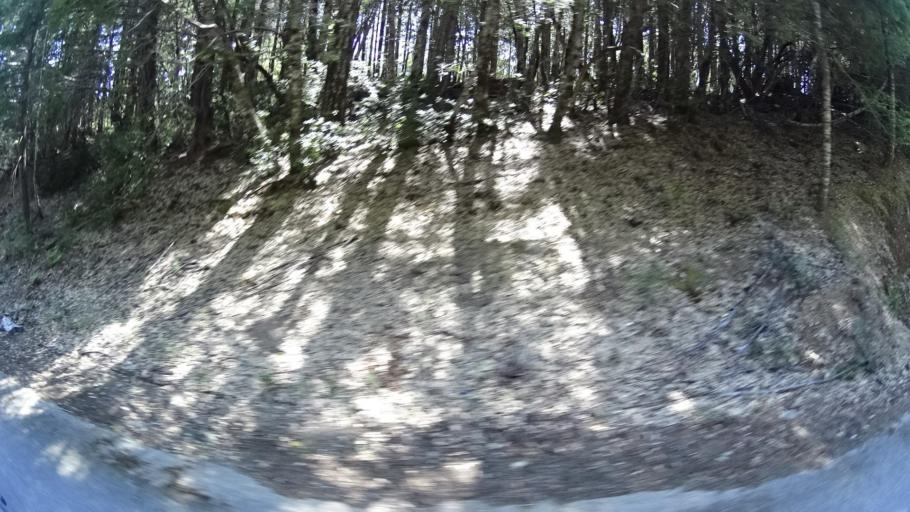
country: US
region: California
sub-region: Humboldt County
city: Redway
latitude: 40.1557
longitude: -124.0542
